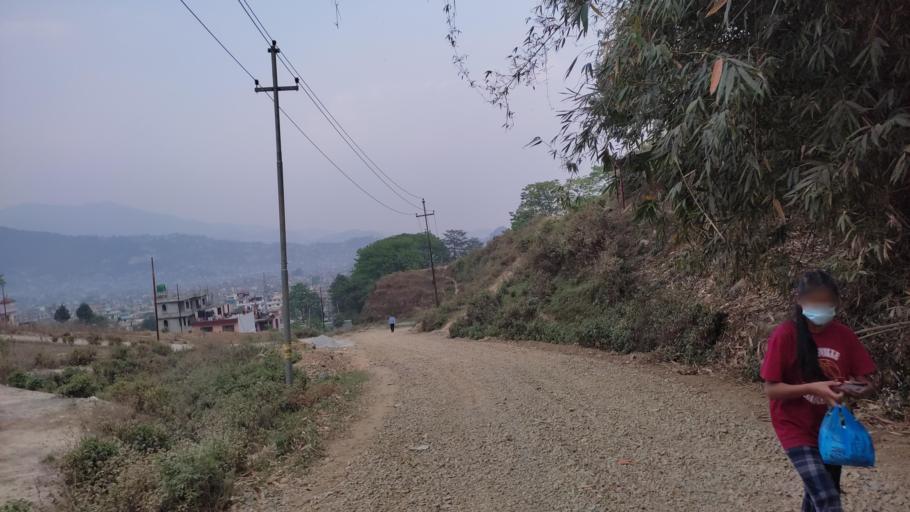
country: NP
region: Central Region
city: Kirtipur
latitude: 27.6741
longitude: 85.2399
